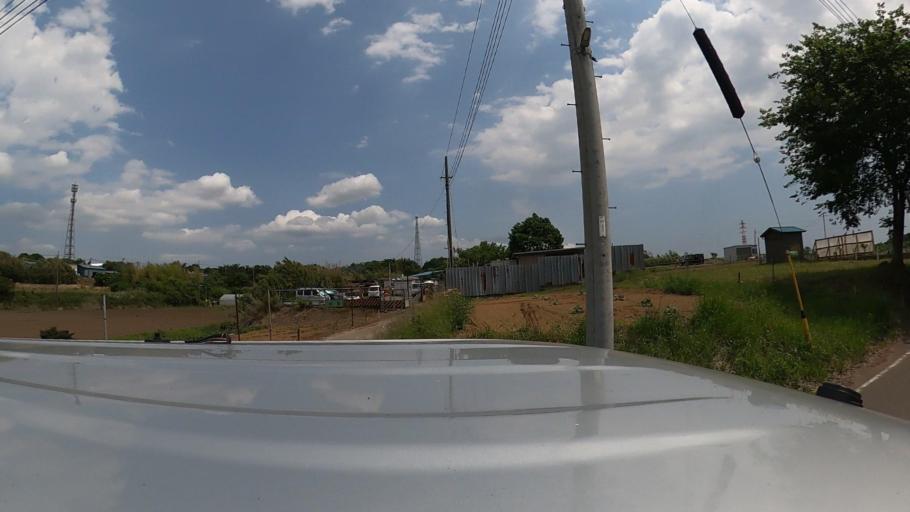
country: JP
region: Kanagawa
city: Chigasaki
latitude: 35.3874
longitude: 139.4186
